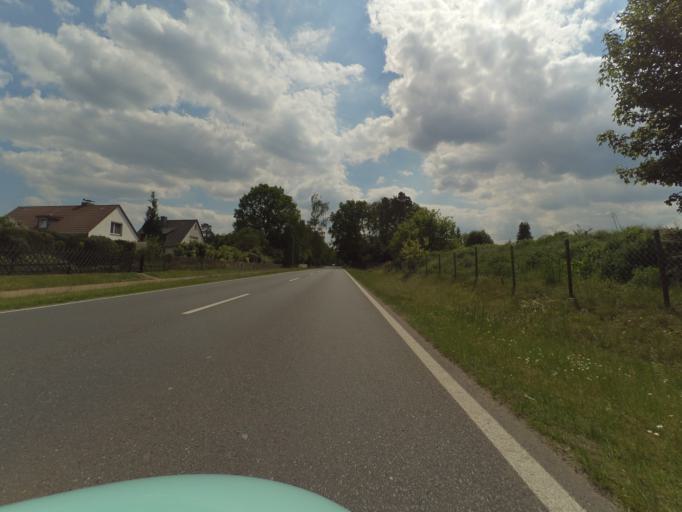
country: DE
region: Lower Saxony
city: Winsen
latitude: 52.6525
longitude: 9.9325
